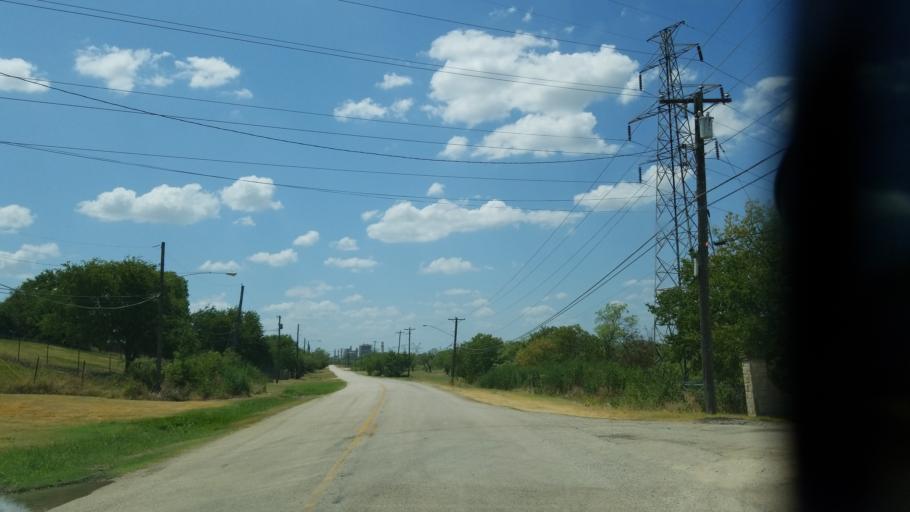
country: US
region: Texas
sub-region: Dallas County
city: Cockrell Hill
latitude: 32.7425
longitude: -96.9273
